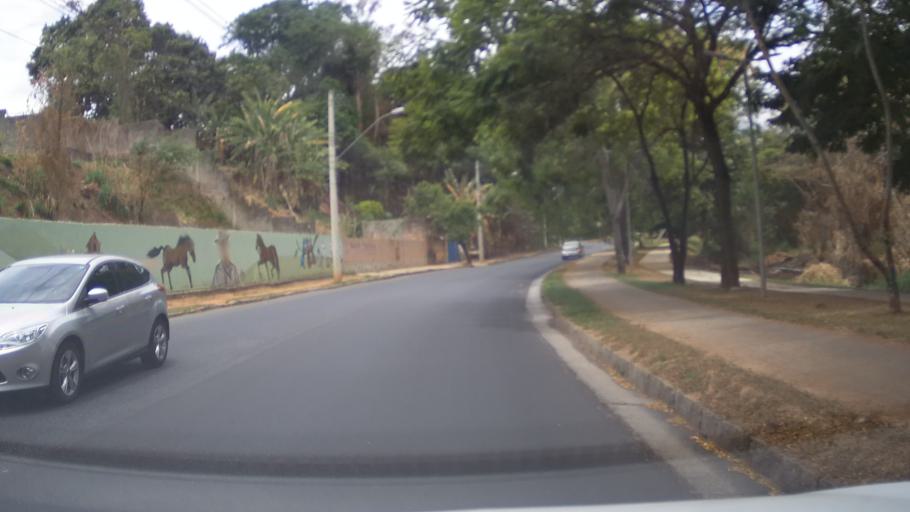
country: BR
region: Minas Gerais
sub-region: Belo Horizonte
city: Belo Horizonte
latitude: -19.8505
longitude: -43.9985
